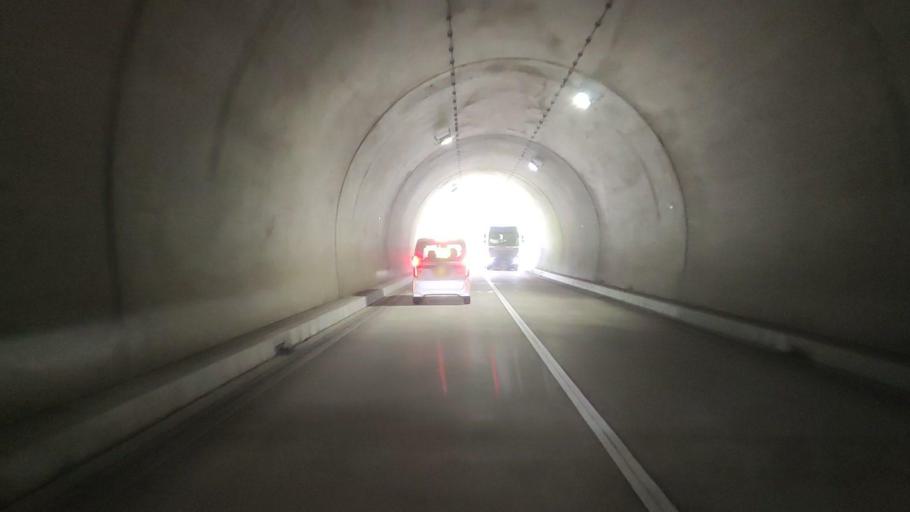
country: JP
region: Wakayama
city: Shingu
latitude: 33.8906
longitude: 135.8798
